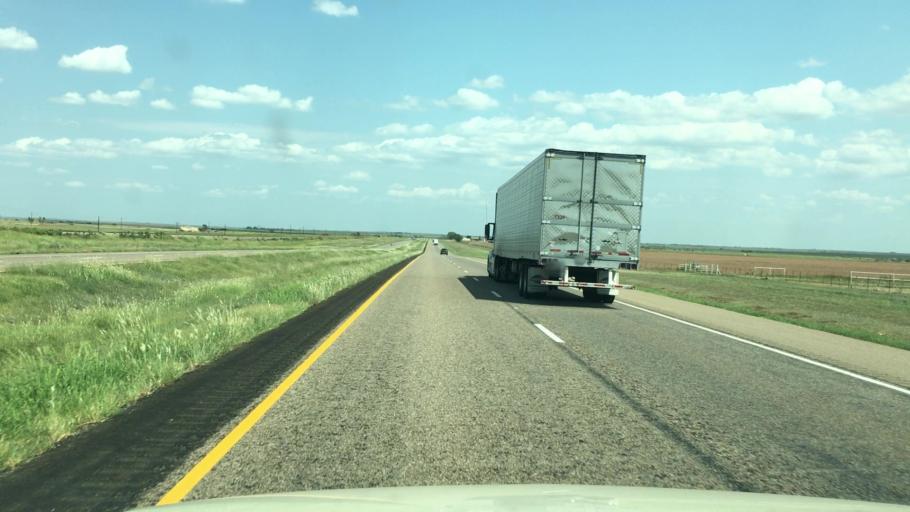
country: US
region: Texas
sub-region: Armstrong County
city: Claude
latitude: 35.0321
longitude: -101.1334
